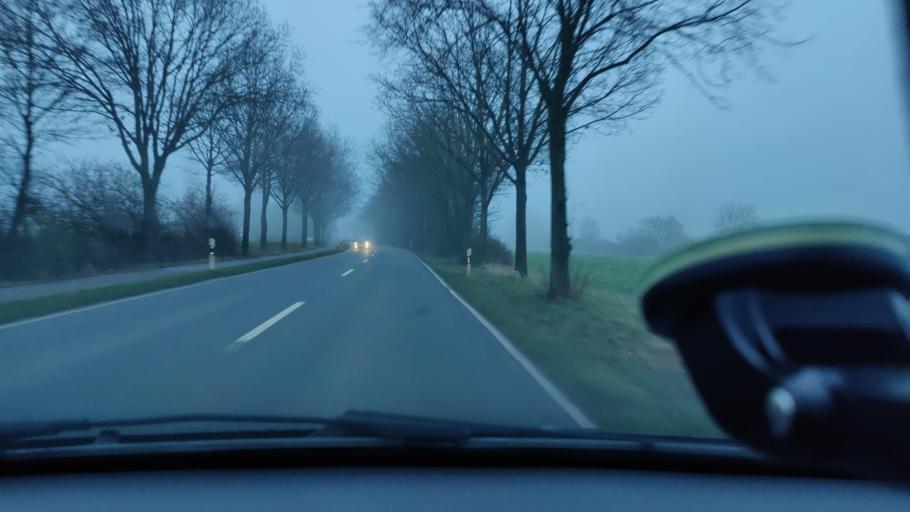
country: DE
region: North Rhine-Westphalia
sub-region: Regierungsbezirk Dusseldorf
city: Mehrhoog
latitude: 51.6839
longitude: 6.5209
